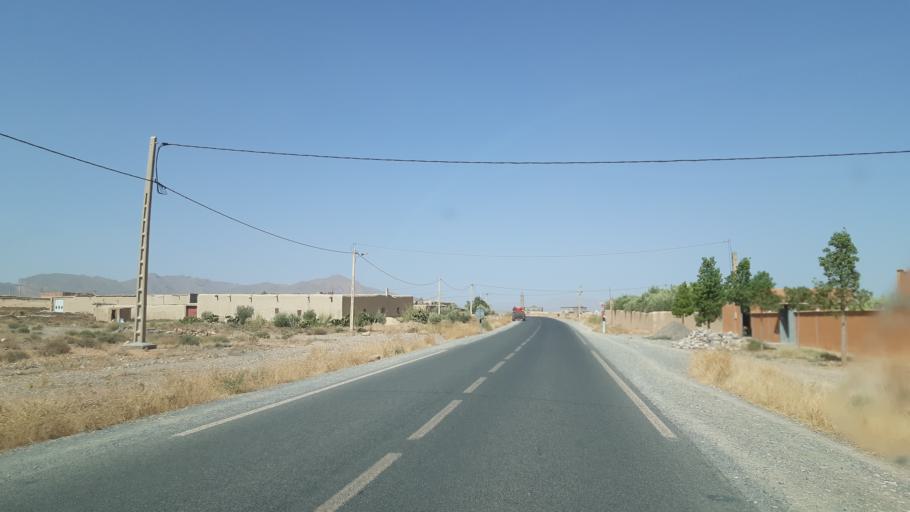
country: MA
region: Meknes-Tafilalet
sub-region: Errachidia
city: Amouguer
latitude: 32.2396
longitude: -4.6047
